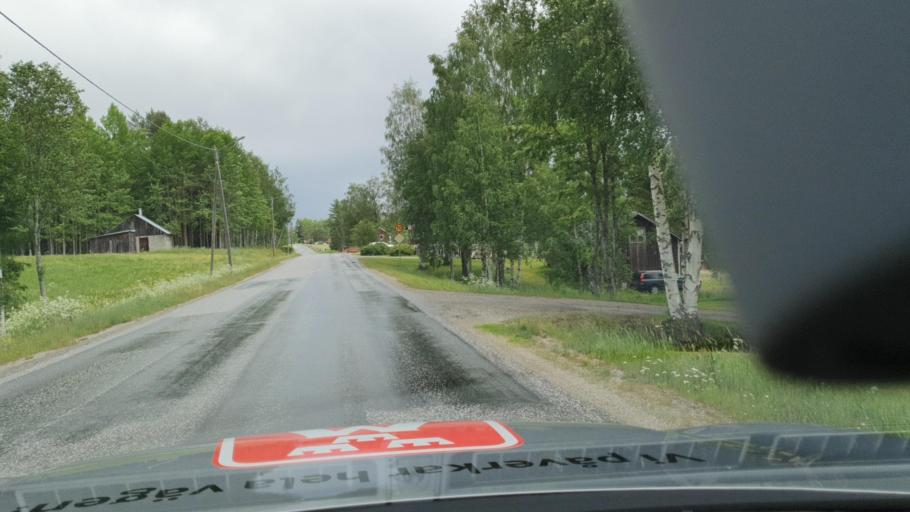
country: SE
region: Vaesternorrland
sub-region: OErnskoeldsviks Kommun
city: Bredbyn
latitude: 63.3316
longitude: 18.0577
